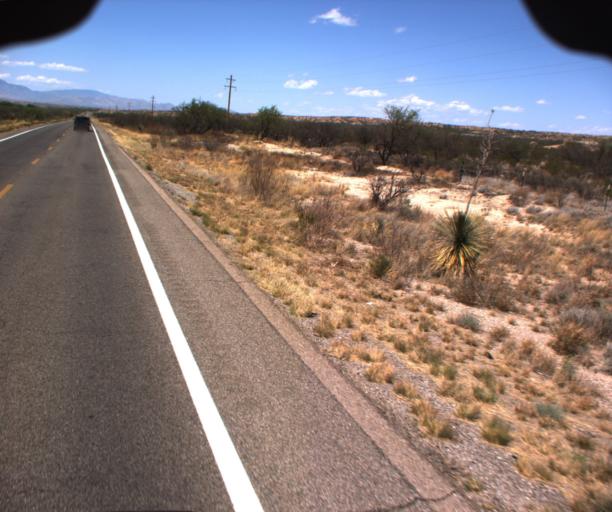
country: US
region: Arizona
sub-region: Cochise County
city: Saint David
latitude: 31.8419
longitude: -110.1908
